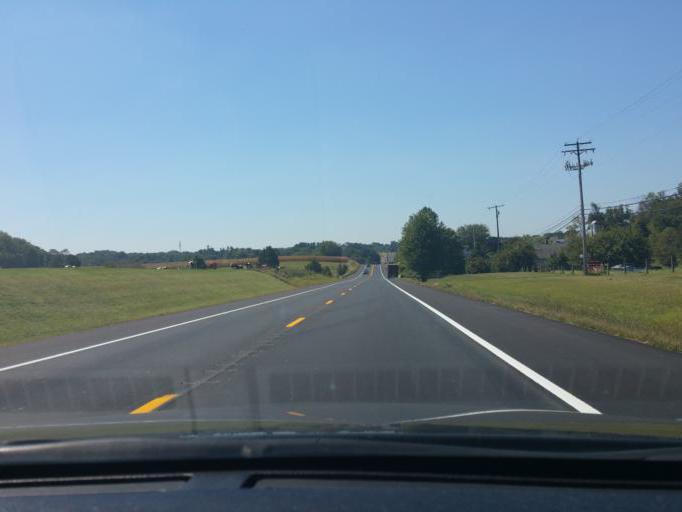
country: US
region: Maryland
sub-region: Harford County
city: Aberdeen
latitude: 39.5705
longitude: -76.2224
